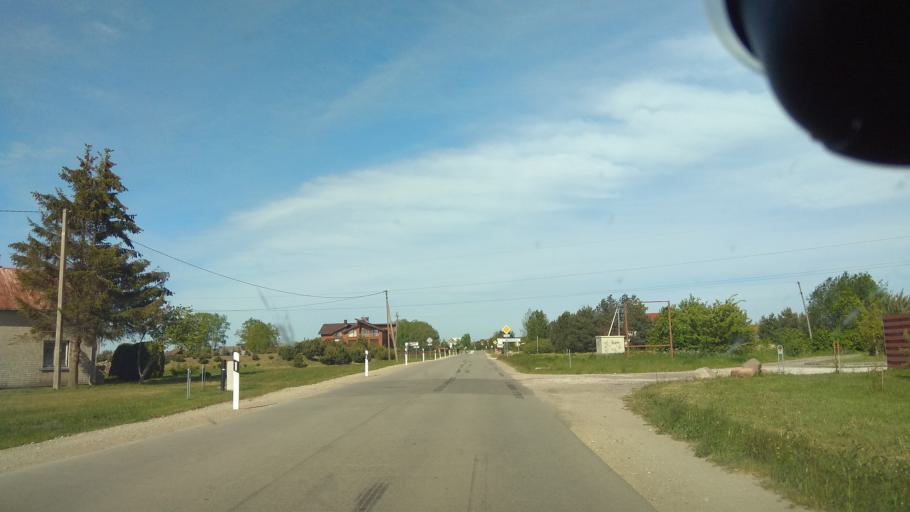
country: LT
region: Klaipedos apskritis
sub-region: Klaipeda
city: Klaipeda
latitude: 55.7542
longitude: 21.1807
